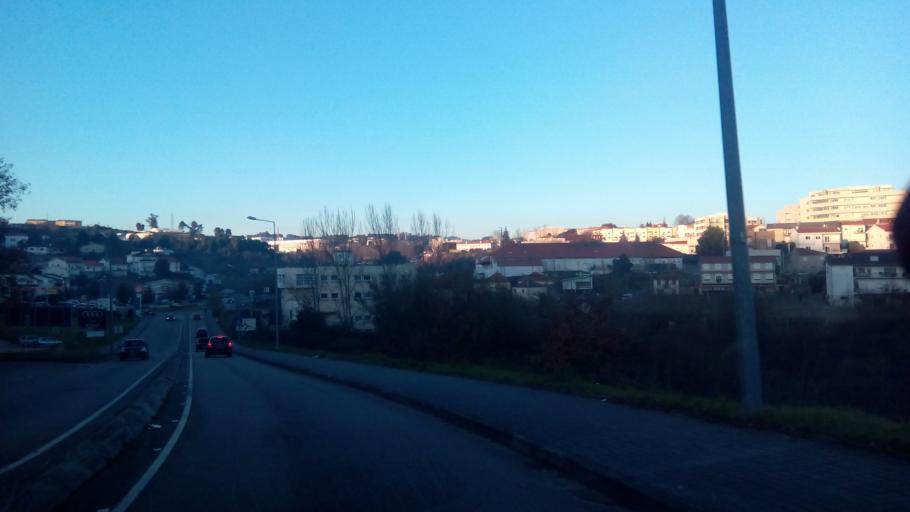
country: PT
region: Porto
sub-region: Amarante
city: Amarante
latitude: 41.2707
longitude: -8.0889
